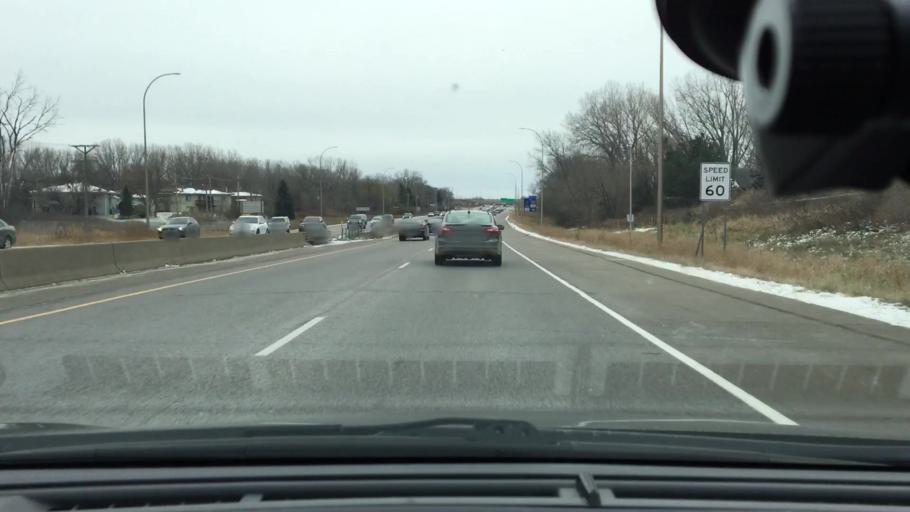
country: US
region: Minnesota
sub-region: Hennepin County
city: New Hope
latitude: 45.0670
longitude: -93.4008
